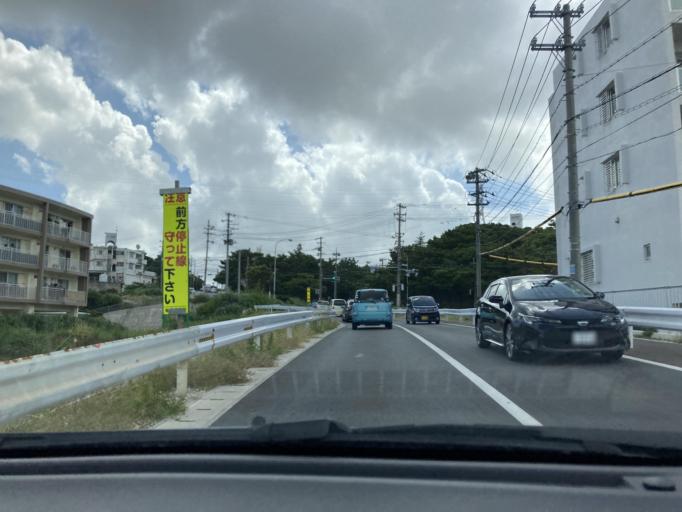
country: JP
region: Okinawa
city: Ginowan
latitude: 26.2580
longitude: 127.7248
